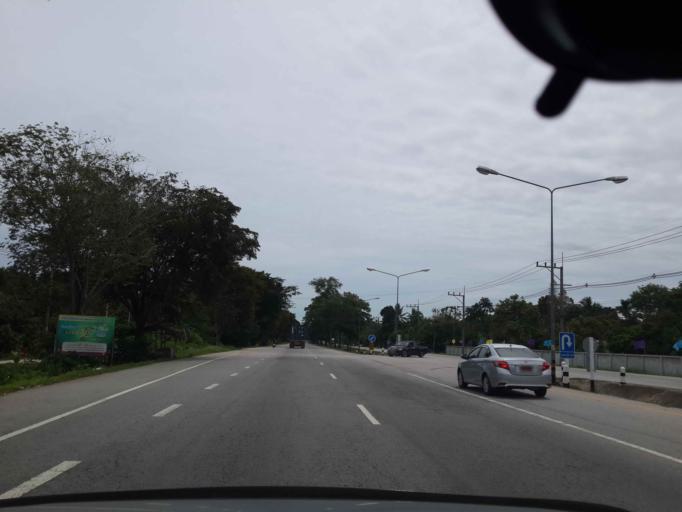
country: TH
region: Narathiwat
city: Yi-ngo
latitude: 6.4045
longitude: 101.7397
